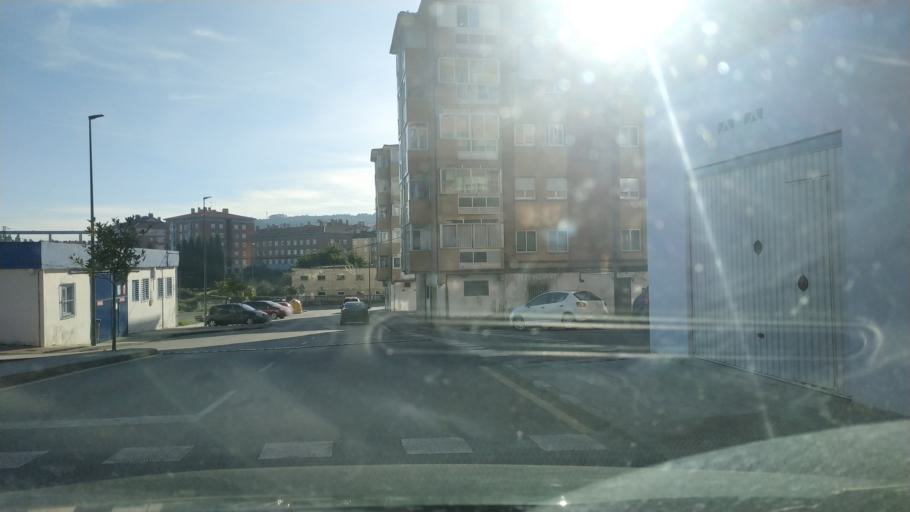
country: ES
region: Asturias
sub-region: Province of Asturias
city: Corvera de Asturias
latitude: 43.5393
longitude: -5.8888
